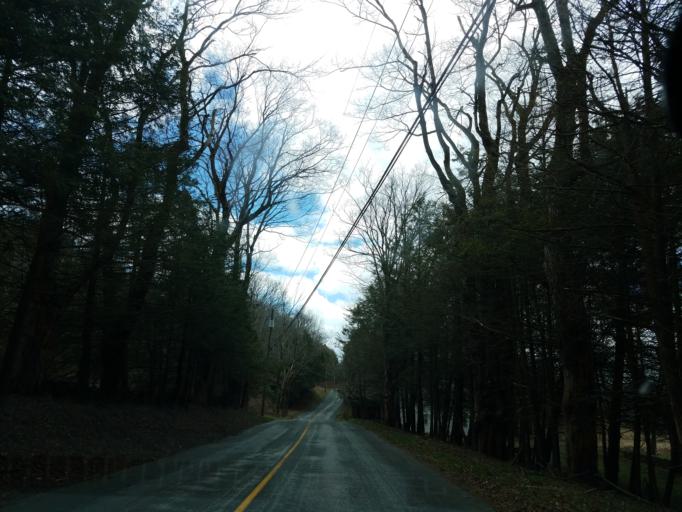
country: US
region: Connecticut
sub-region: Litchfield County
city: Litchfield
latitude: 41.7828
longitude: -73.1774
